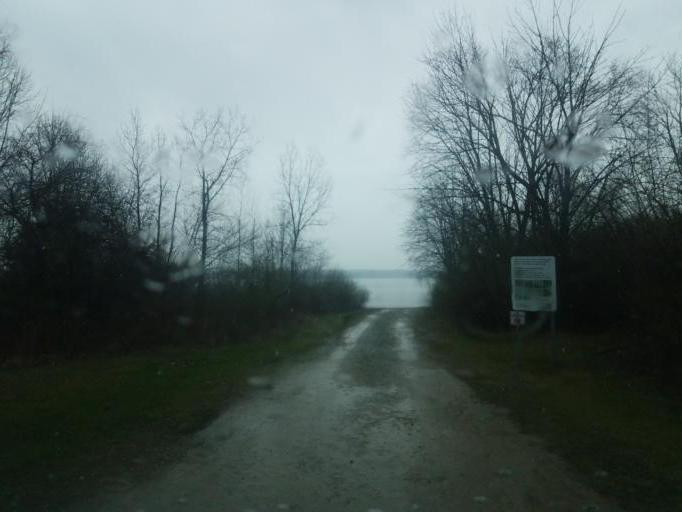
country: US
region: Ohio
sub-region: Delaware County
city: Lewis Center
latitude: 40.1980
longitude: -82.9706
